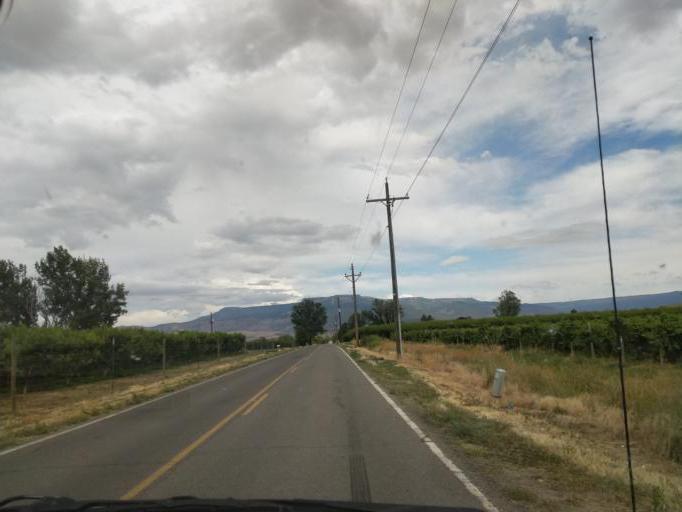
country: US
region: Colorado
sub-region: Mesa County
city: Clifton
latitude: 39.0558
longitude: -108.4365
